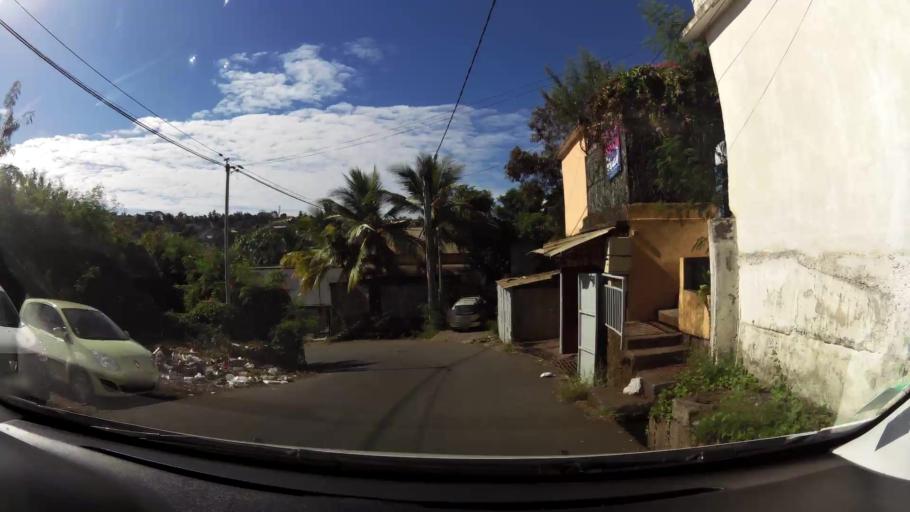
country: YT
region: Mamoudzou
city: Mamoudzou
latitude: -12.7855
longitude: 45.2224
